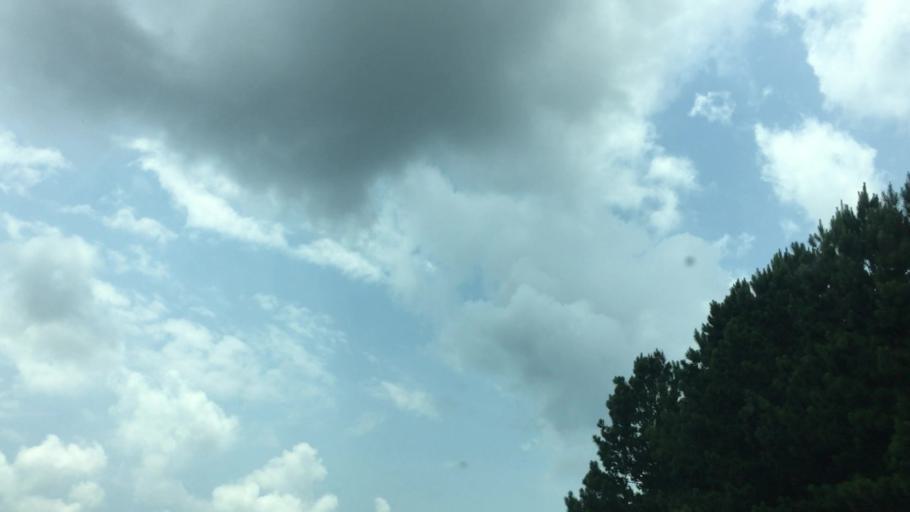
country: US
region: Georgia
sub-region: Fulton County
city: Palmetto
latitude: 33.5784
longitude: -84.6711
